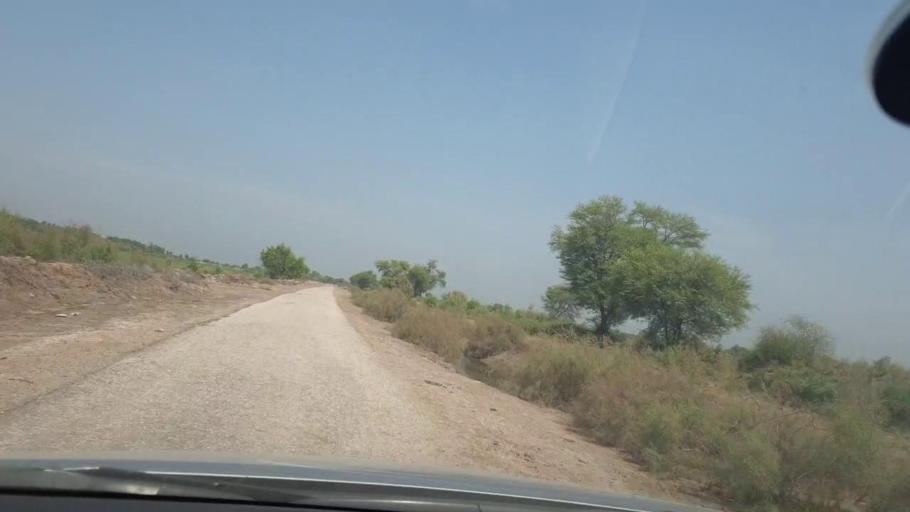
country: PK
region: Balochistan
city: Mehrabpur
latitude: 28.0816
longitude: 68.0420
